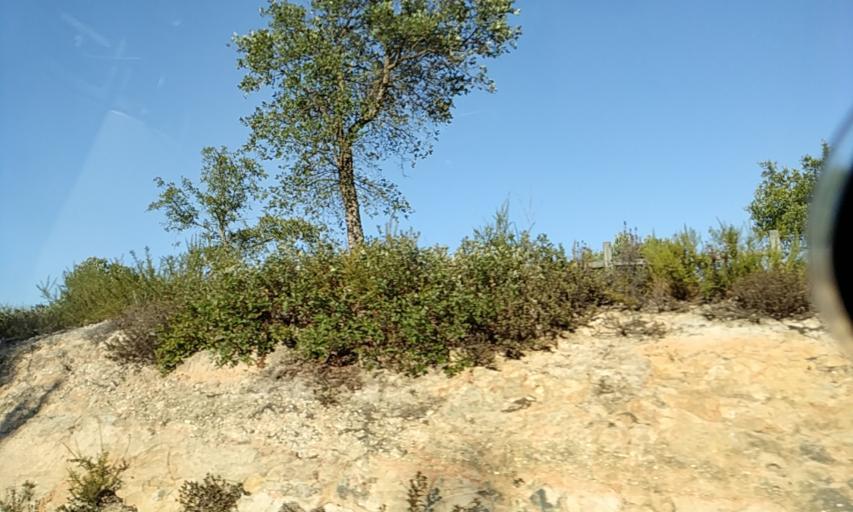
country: PT
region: Santarem
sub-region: Almeirim
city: Fazendas de Almeirim
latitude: 39.0754
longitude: -8.5663
